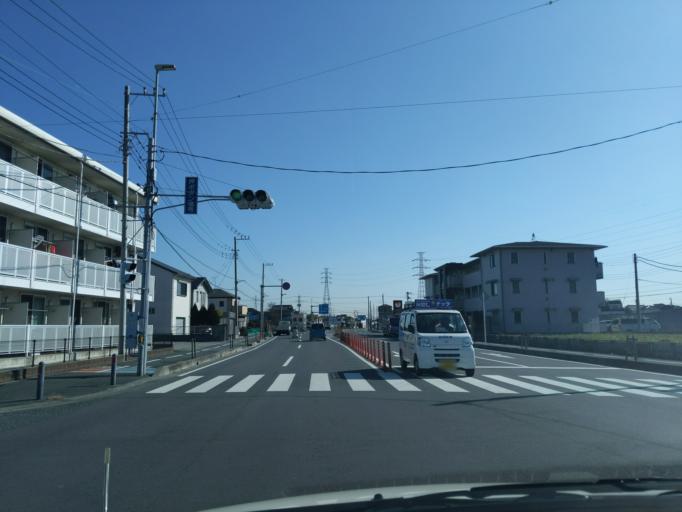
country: JP
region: Saitama
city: Yashio-shi
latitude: 35.8140
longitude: 139.8562
